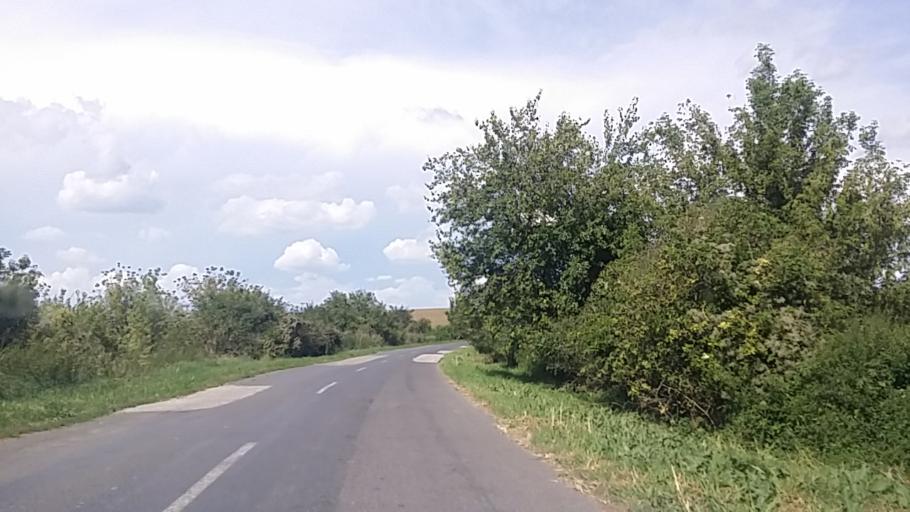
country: HU
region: Tolna
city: Hogyesz
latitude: 46.5168
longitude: 18.4054
